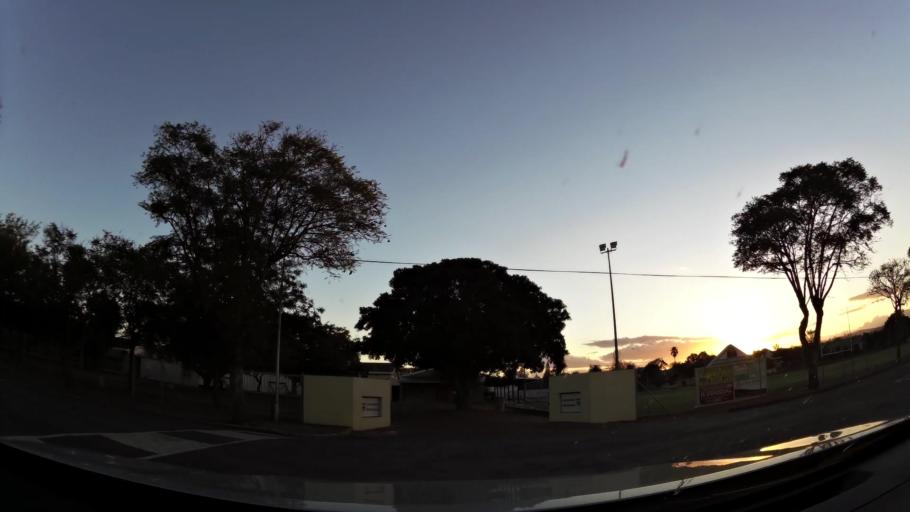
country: ZA
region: Western Cape
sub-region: Eden District Municipality
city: Riversdale
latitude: -34.0893
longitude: 21.2579
